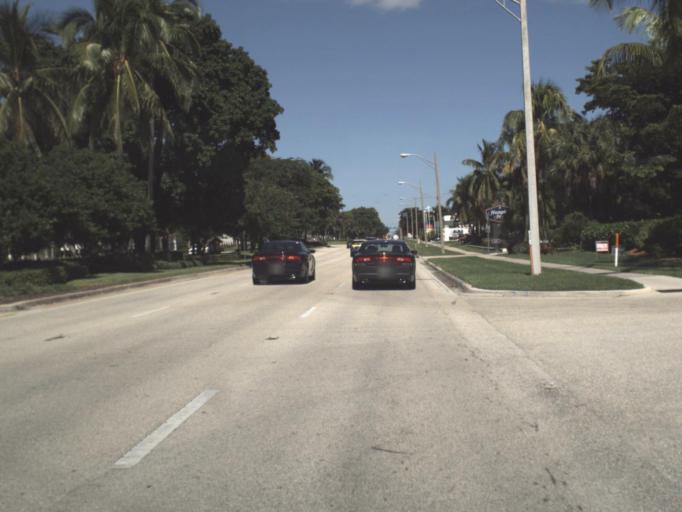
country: US
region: Florida
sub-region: Collier County
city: Naples
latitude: 26.1842
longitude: -81.7997
